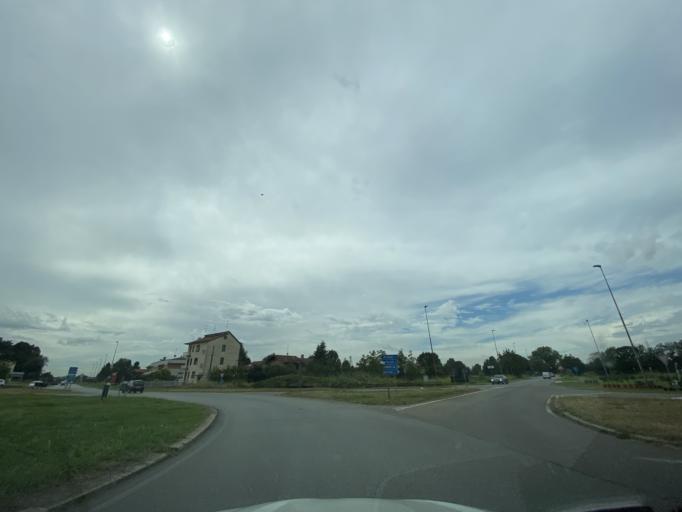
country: IT
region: Lombardy
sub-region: Citta metropolitana di Milano
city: Pessano Con Bornago
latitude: 45.5429
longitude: 9.3920
